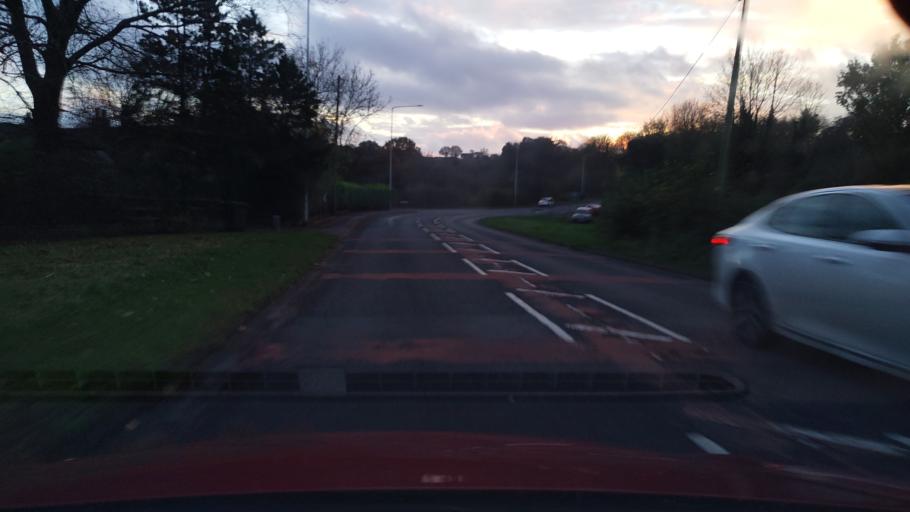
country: GB
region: England
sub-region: Lancashire
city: Clayton-le-Woods
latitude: 53.7009
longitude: -2.6536
